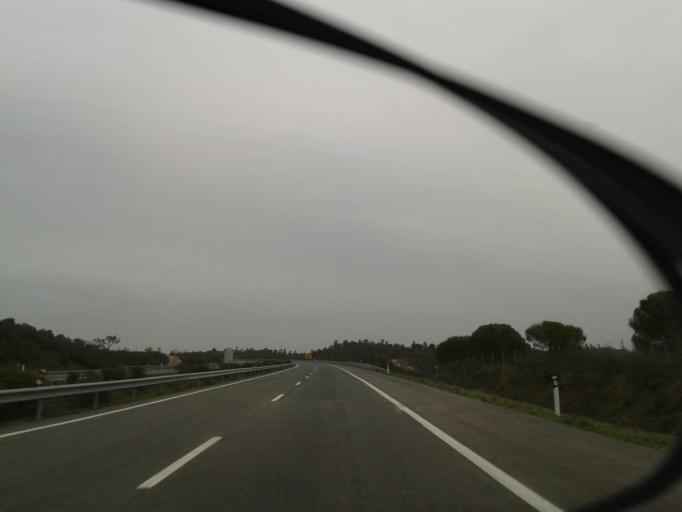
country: PT
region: Faro
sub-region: Silves
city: Sao Bartolomeu de Messines
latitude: 37.2678
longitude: -8.2594
